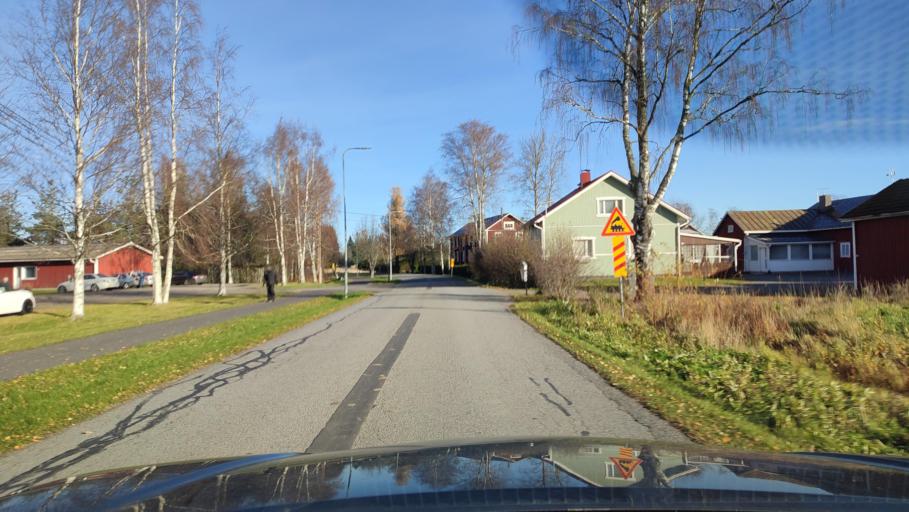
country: FI
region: Southern Ostrobothnia
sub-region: Suupohja
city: Teuva
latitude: 62.4753
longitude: 21.7499
